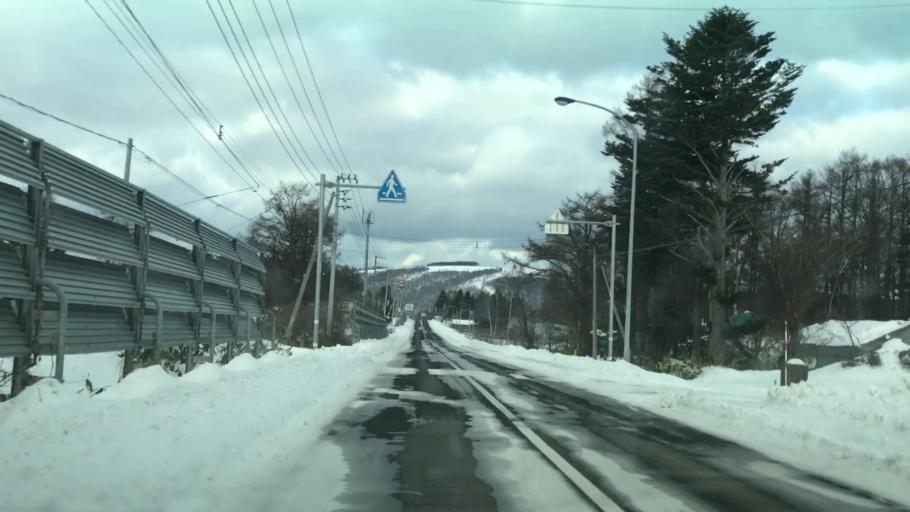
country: JP
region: Hokkaido
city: Yoichi
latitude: 43.3103
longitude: 140.5494
